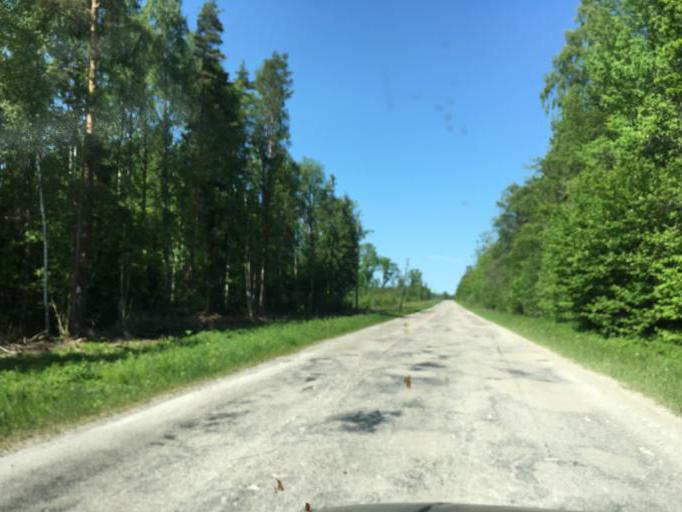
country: LV
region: Dundaga
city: Dundaga
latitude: 57.4555
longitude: 22.3215
